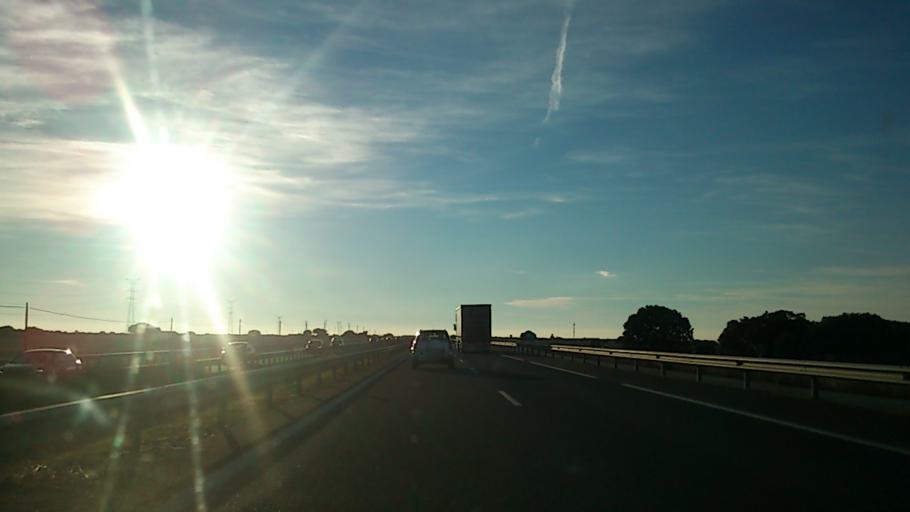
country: ES
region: Castille-La Mancha
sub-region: Provincia de Guadalajara
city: Gajanejos
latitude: 40.8476
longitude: -2.8690
